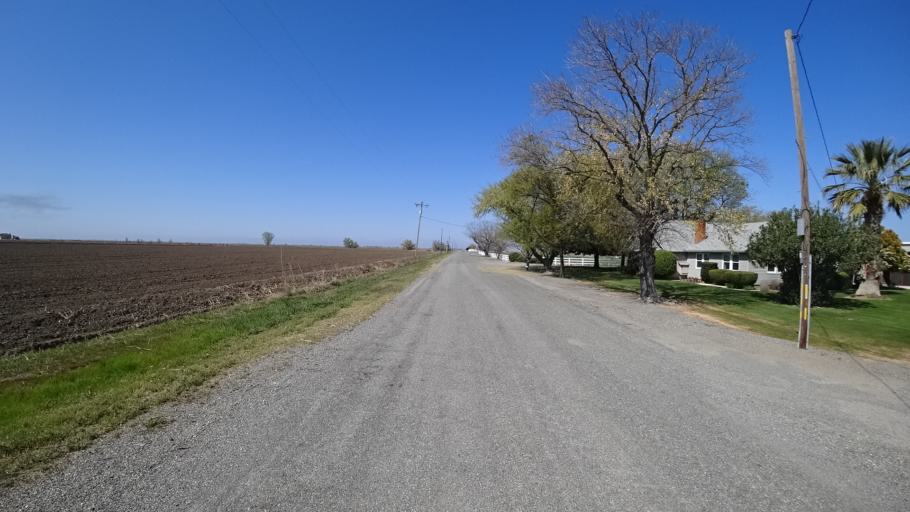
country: US
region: California
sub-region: Glenn County
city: Willows
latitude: 39.4430
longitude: -122.0389
